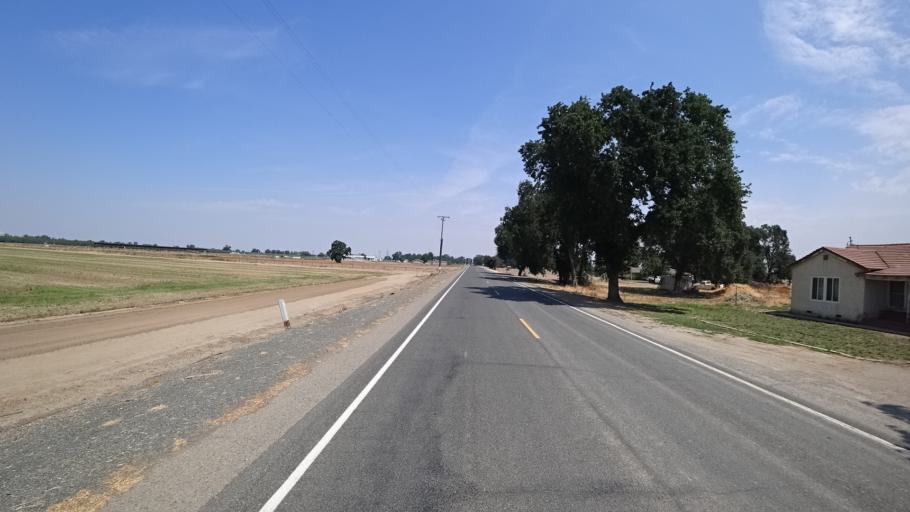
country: US
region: California
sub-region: Kings County
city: Lemoore
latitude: 36.3574
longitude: -119.7810
